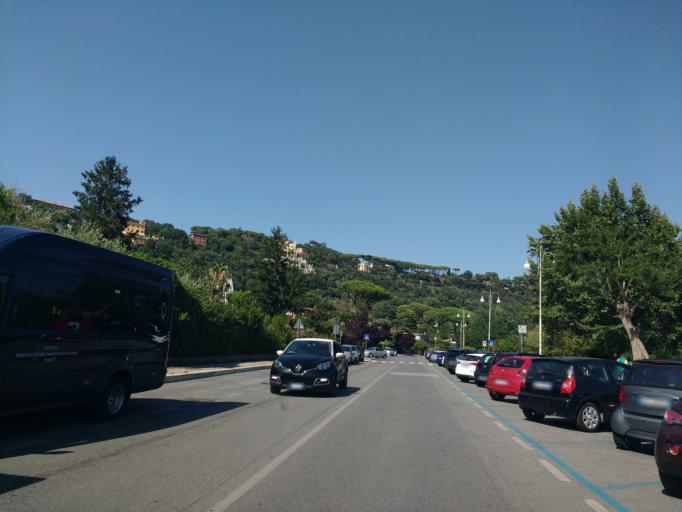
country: IT
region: Latium
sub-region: Citta metropolitana di Roma Capitale
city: Castel Gandolfo
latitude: 41.7599
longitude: 12.6557
